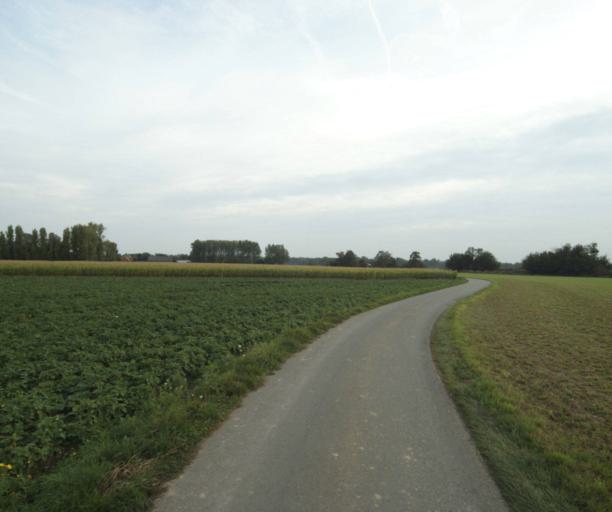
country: FR
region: Nord-Pas-de-Calais
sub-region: Departement du Nord
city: Avelin
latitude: 50.5496
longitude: 3.0707
